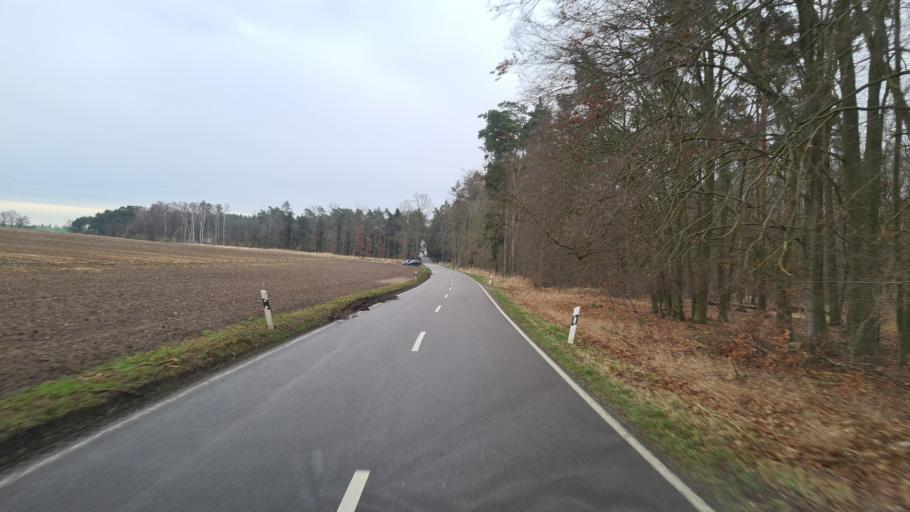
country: DE
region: Brandenburg
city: Gransee
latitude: 52.9376
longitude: 13.2325
